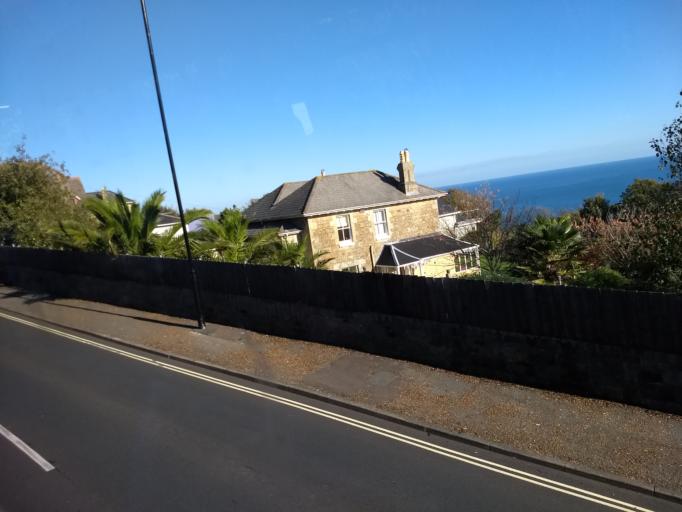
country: GB
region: England
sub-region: Isle of Wight
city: Ventnor
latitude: 50.6026
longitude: -1.1844
